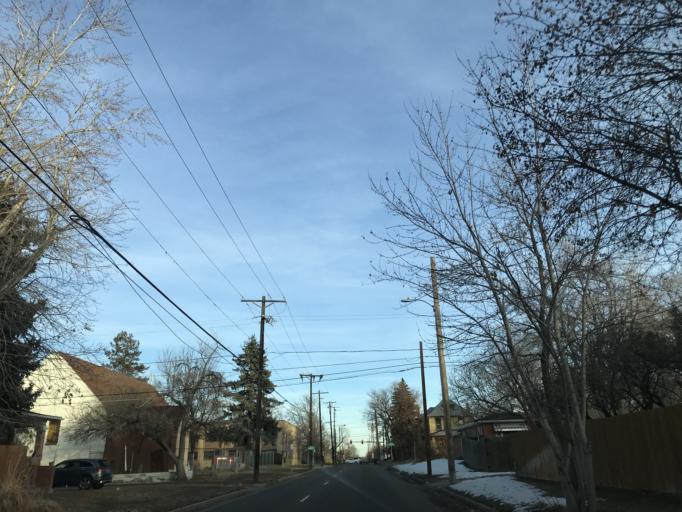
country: US
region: Colorado
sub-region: Arapahoe County
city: Glendale
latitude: 39.7387
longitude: -104.9057
